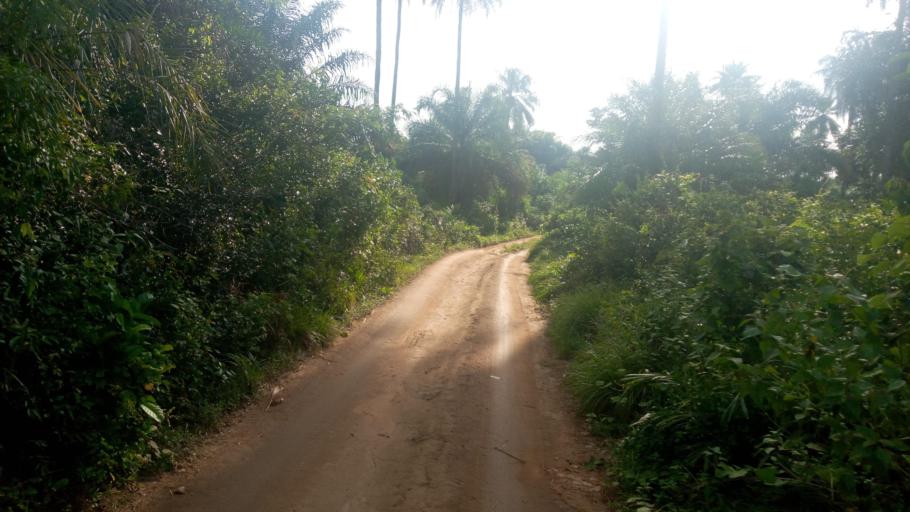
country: SL
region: Southern Province
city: Serabu
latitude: 7.6424
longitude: -12.1586
